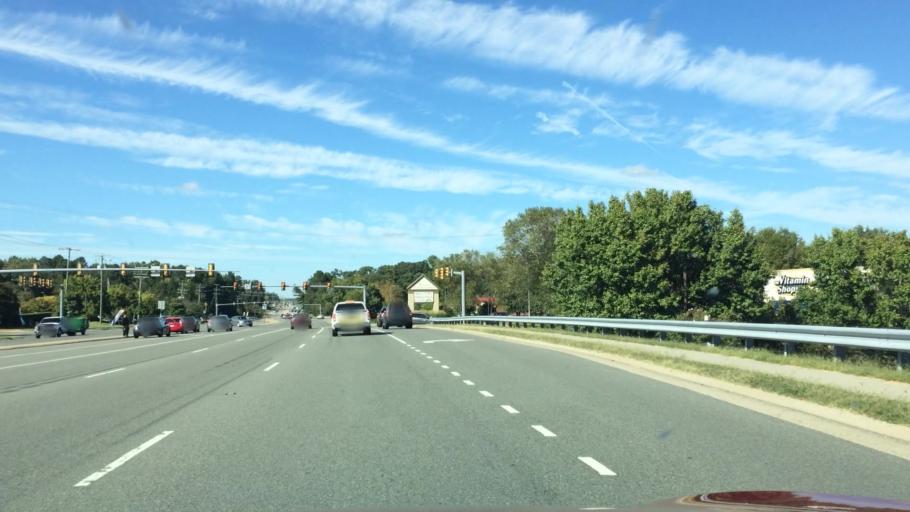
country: US
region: Virginia
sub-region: Henrico County
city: Glen Allen
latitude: 37.6735
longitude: -77.4605
